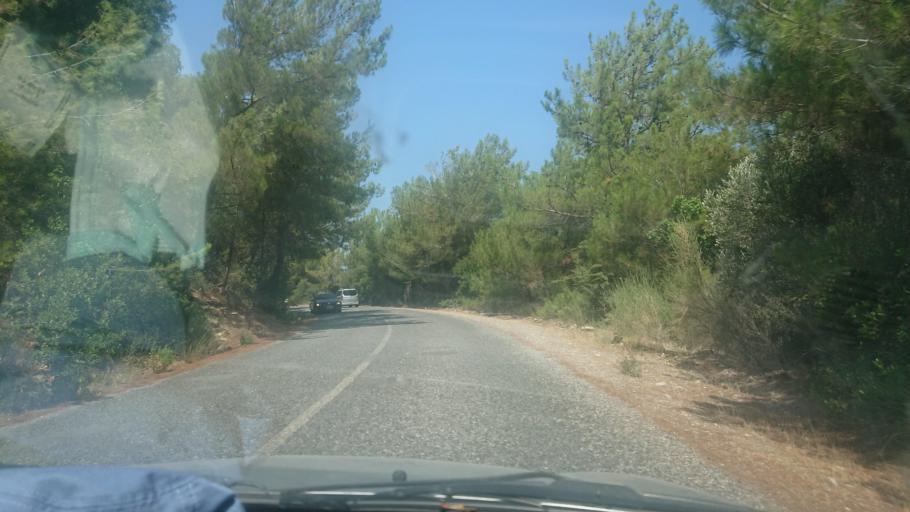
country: TR
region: Aydin
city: Atburgazi
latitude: 37.6971
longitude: 27.1773
